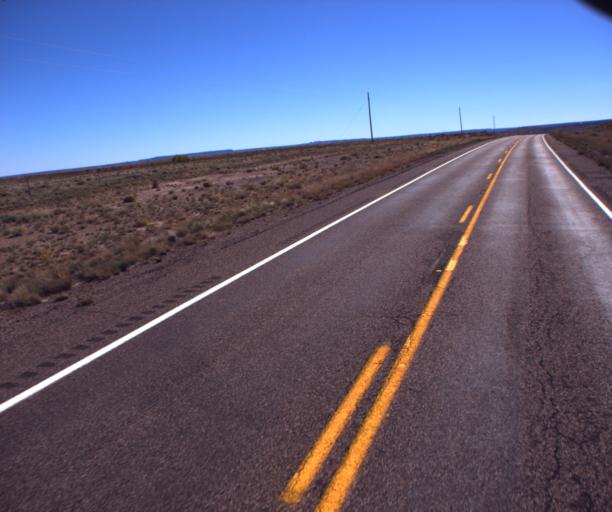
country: US
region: Arizona
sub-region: Apache County
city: Saint Johns
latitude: 34.5345
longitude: -109.4632
